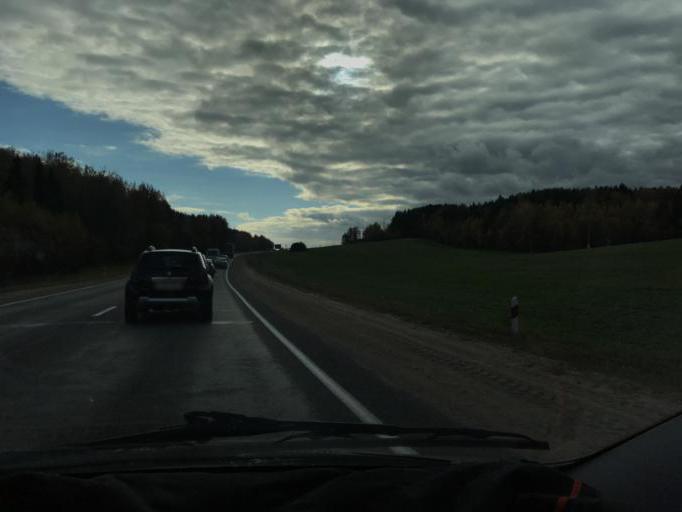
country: BY
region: Minsk
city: Lahoysk
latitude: 54.2183
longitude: 27.8315
